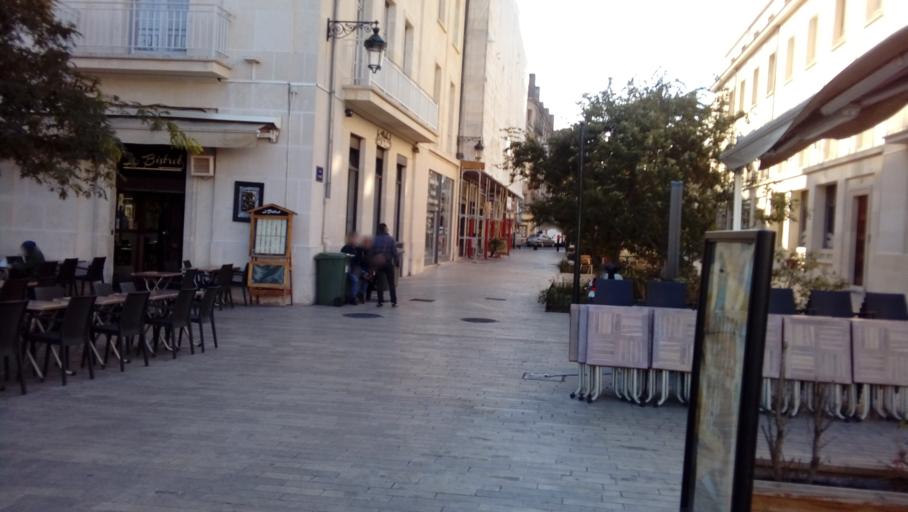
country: FR
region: Centre
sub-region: Departement du Loiret
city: Orleans
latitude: 47.9024
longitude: 1.9033
